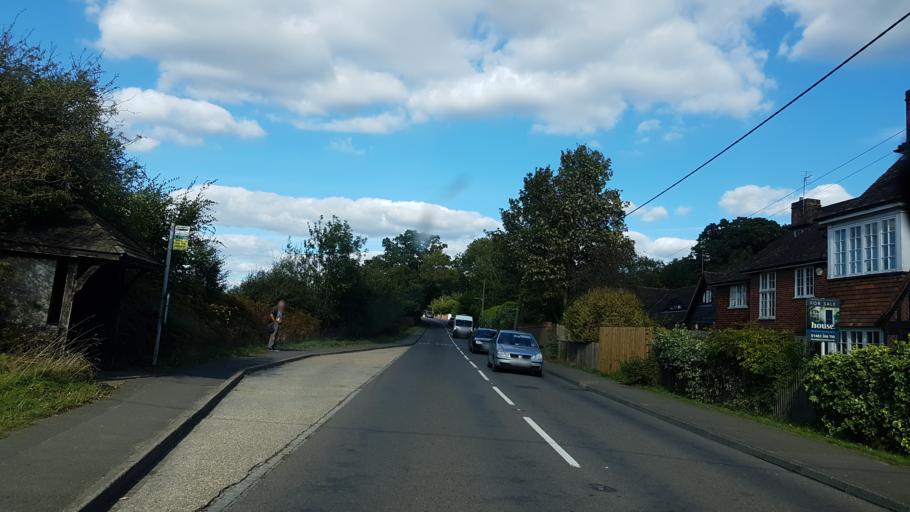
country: GB
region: England
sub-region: Surrey
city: Chiddingfold
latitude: 51.1146
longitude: -0.6273
